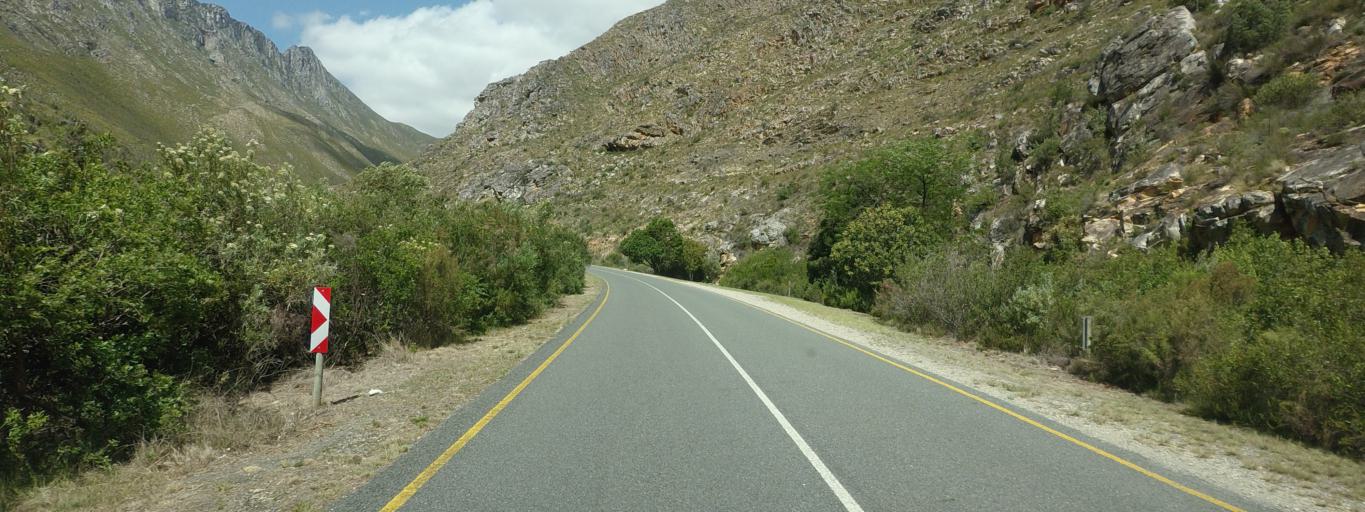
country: ZA
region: Western Cape
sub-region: Overberg District Municipality
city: Swellendam
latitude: -33.9486
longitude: 20.7051
